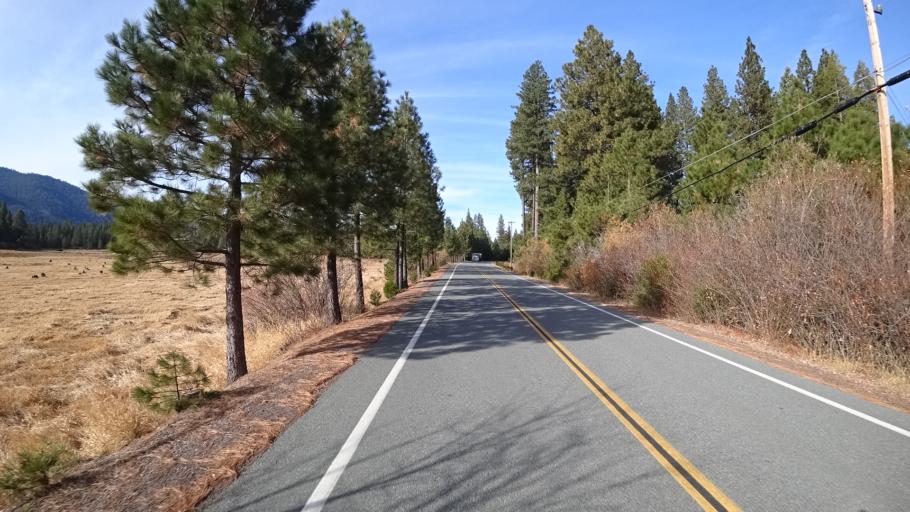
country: US
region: California
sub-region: Siskiyou County
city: Weed
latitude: 41.3846
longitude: -122.4081
